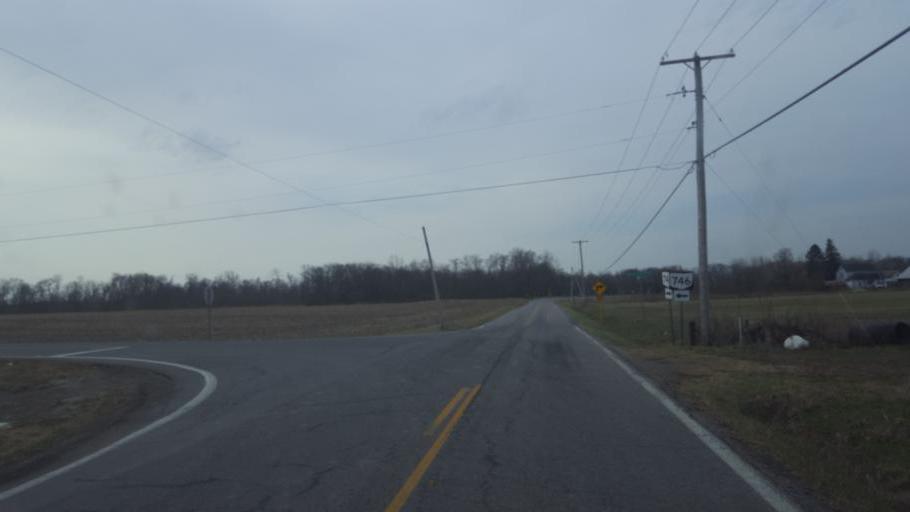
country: US
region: Ohio
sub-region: Morrow County
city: Cardington
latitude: 40.6239
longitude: -82.9673
